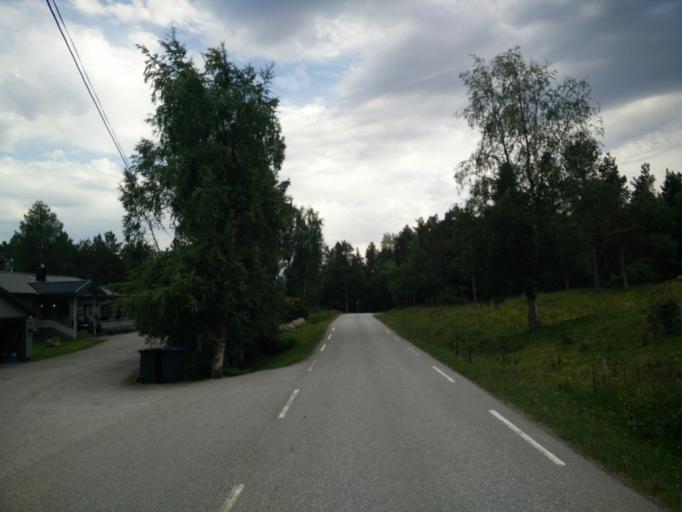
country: NO
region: More og Romsdal
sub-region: Kristiansund
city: Rensvik
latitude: 63.0352
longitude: 7.9551
